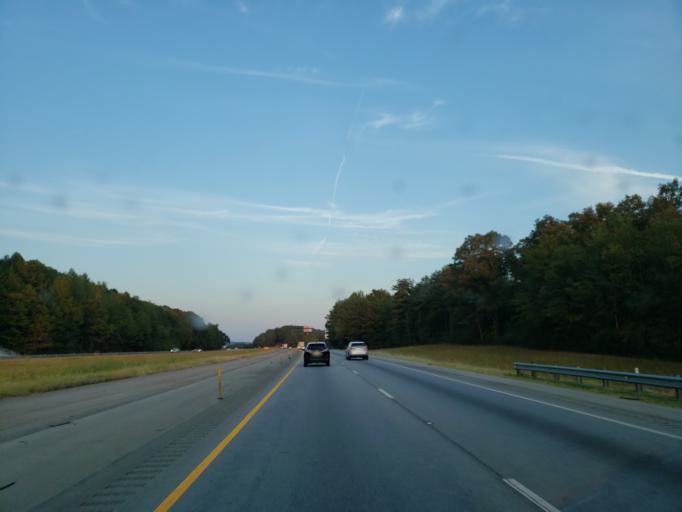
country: US
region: Alabama
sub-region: Calhoun County
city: Oxford
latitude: 33.6105
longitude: -85.7636
